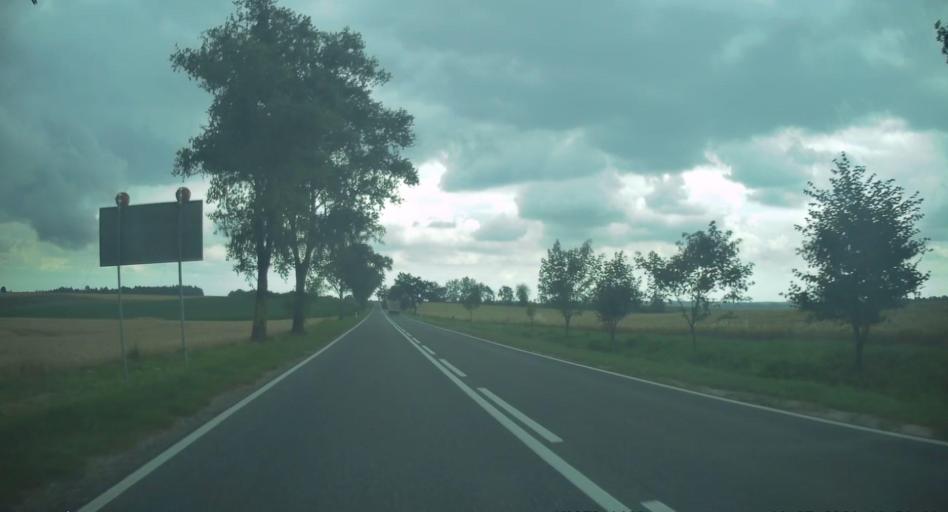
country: PL
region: Opole Voivodeship
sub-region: Powiat nyski
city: Nysa
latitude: 50.4227
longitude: 17.4485
